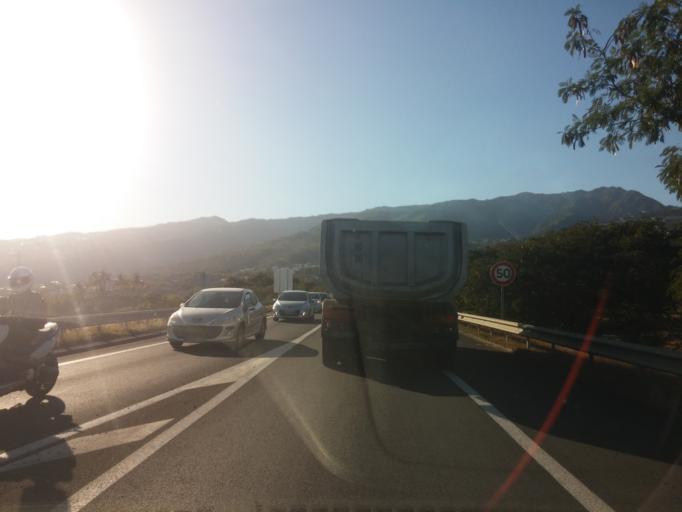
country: RE
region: Reunion
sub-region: Reunion
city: La Possession
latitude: -20.9454
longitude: 55.3236
